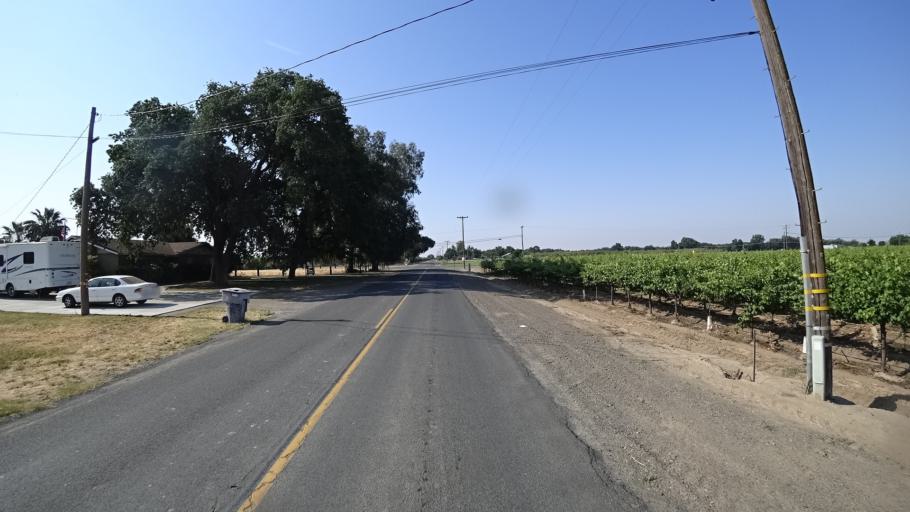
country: US
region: California
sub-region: Kings County
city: Lemoore
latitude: 36.3448
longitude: -119.8340
